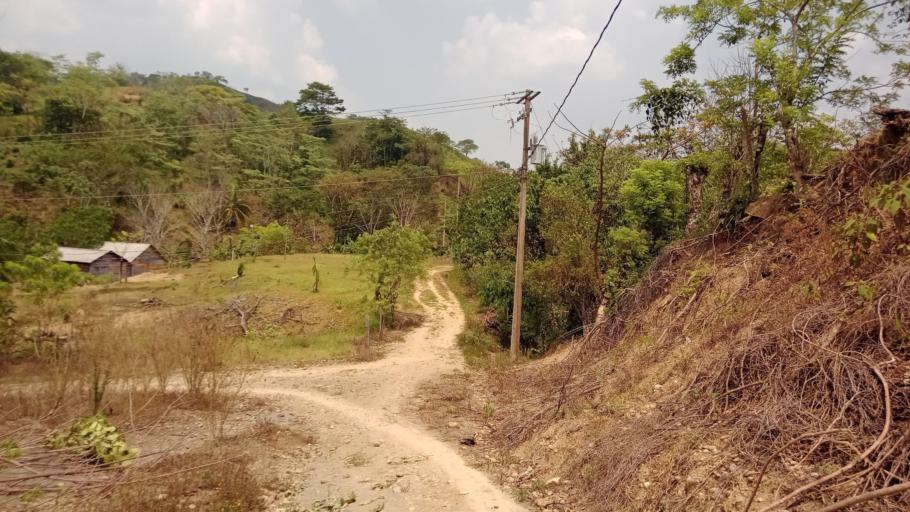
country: MX
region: Tabasco
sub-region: Huimanguillo
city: Francisco Rueda
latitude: 17.5889
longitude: -93.8568
